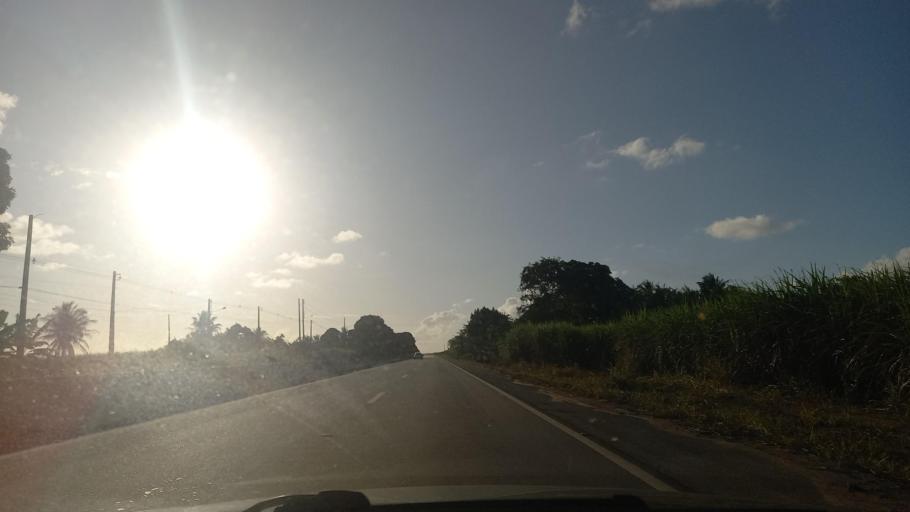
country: BR
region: Alagoas
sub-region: Campo Alegre
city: Campo Alegre
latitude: -9.8177
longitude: -36.2488
